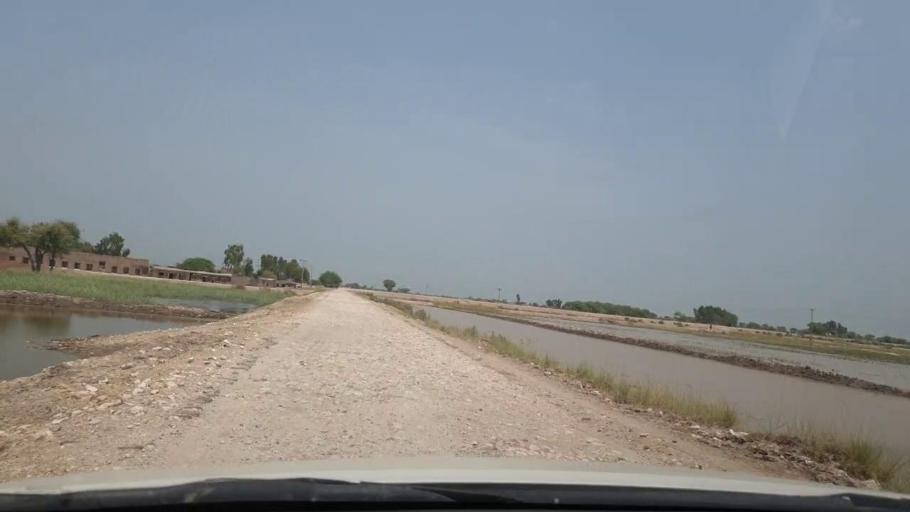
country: PK
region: Sindh
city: Rustam jo Goth
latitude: 28.0765
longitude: 68.8180
